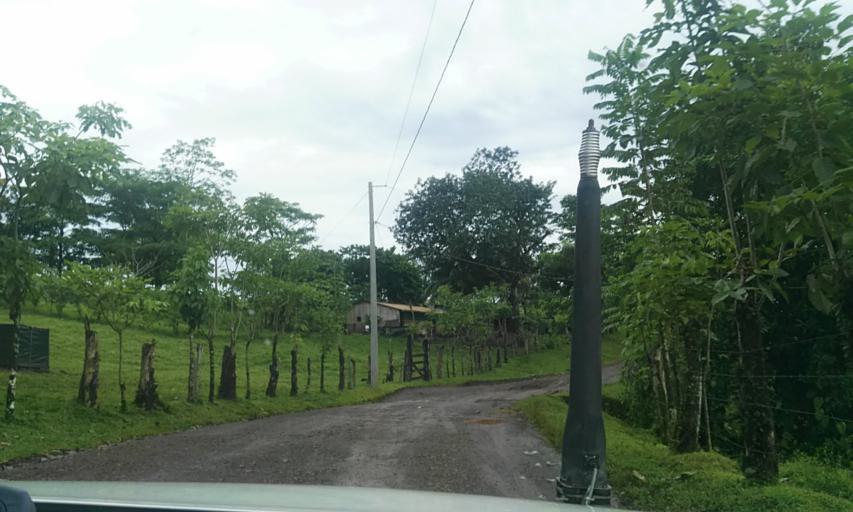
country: NI
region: Matagalpa
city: Rio Blanco
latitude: 12.9547
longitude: -85.1791
